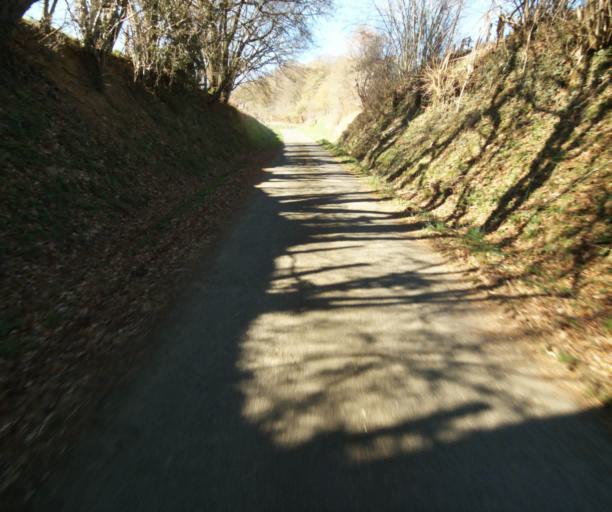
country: FR
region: Limousin
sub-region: Departement de la Correze
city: Chamboulive
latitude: 45.4157
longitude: 1.7025
